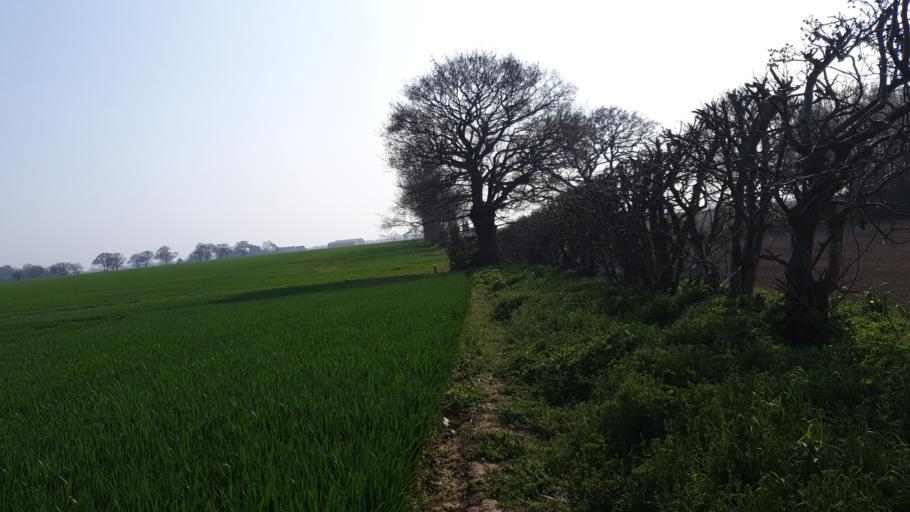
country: GB
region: England
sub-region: Essex
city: Mistley
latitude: 51.8984
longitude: 1.1233
